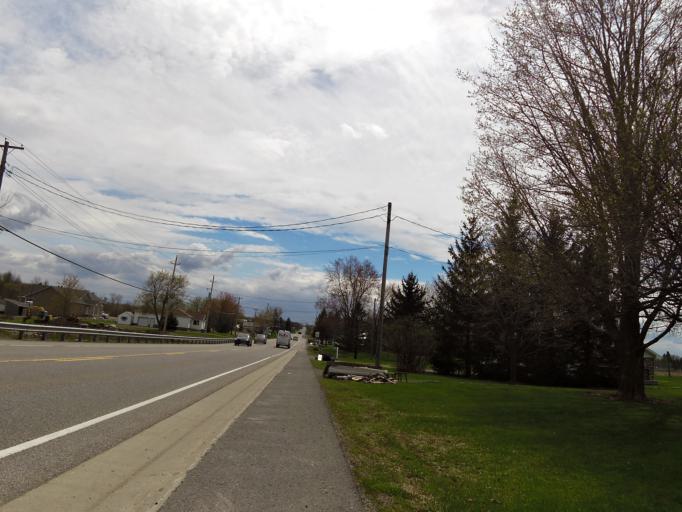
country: CA
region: Ontario
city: Hawkesbury
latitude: 45.5400
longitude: -74.6415
